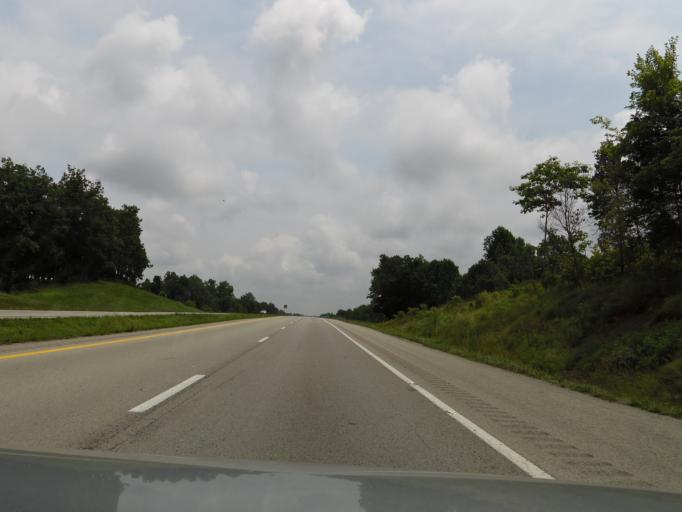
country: US
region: Kentucky
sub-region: Grayson County
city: Leitchfield
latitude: 37.4745
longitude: -86.2497
